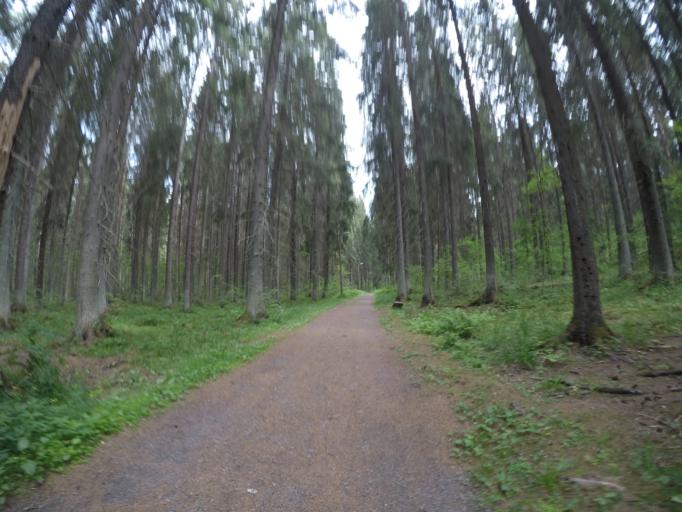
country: FI
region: Haeme
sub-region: Haemeenlinna
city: Haemeenlinna
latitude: 61.0004
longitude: 24.4055
